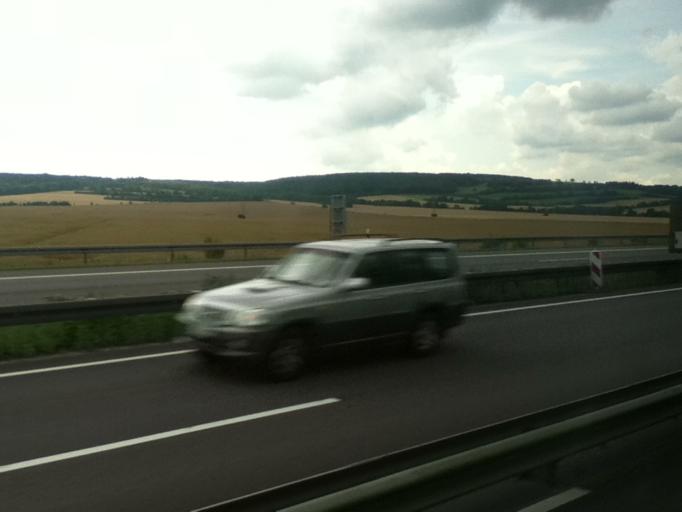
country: DE
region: Thuringia
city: Seebergen
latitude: 50.8790
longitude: 10.8013
